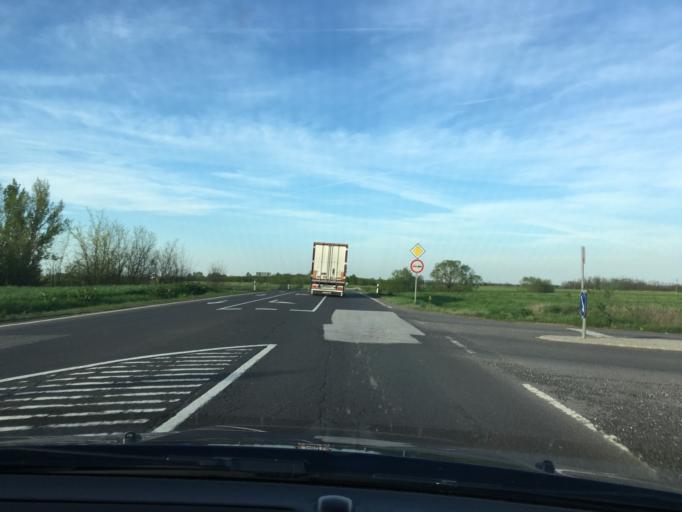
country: HU
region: Hajdu-Bihar
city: Berettyoujfalu
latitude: 47.1670
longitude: 21.5129
